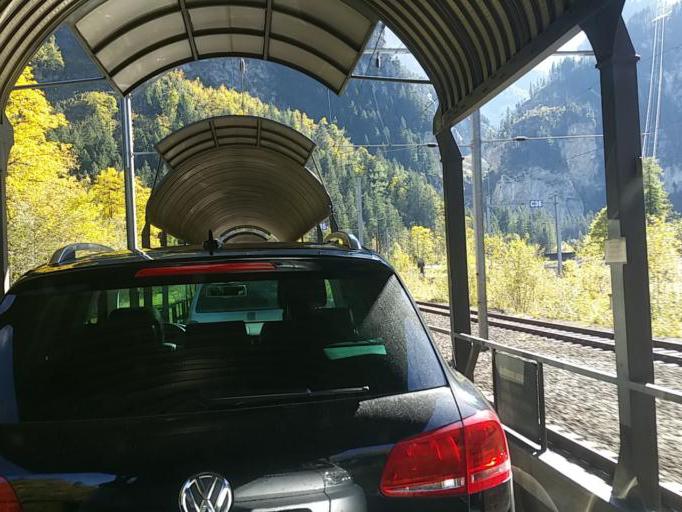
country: CH
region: Bern
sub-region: Frutigen-Niedersimmental District
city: Kandersteg
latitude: 46.4809
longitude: 7.6659
